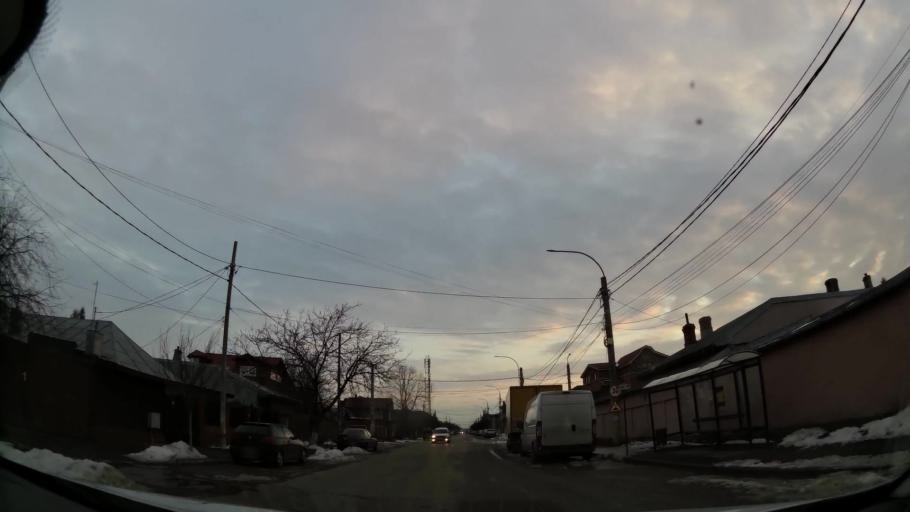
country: RO
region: Ilfov
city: Dobroesti
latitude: 44.4564
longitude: 26.1853
